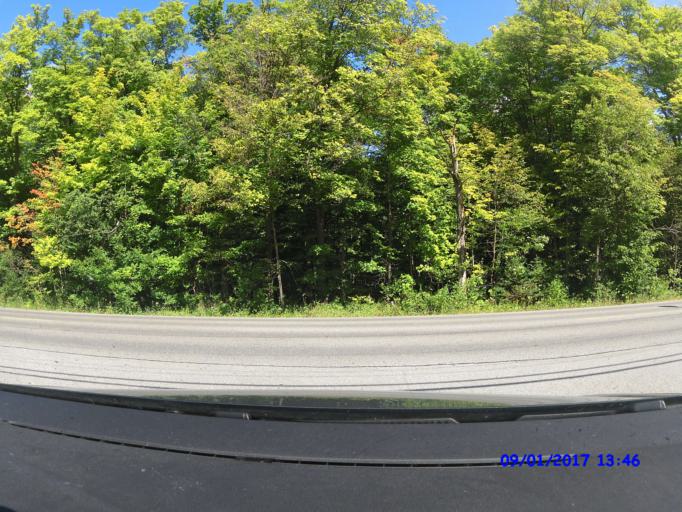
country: CA
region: Ontario
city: Bells Corners
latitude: 45.3661
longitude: -75.9720
